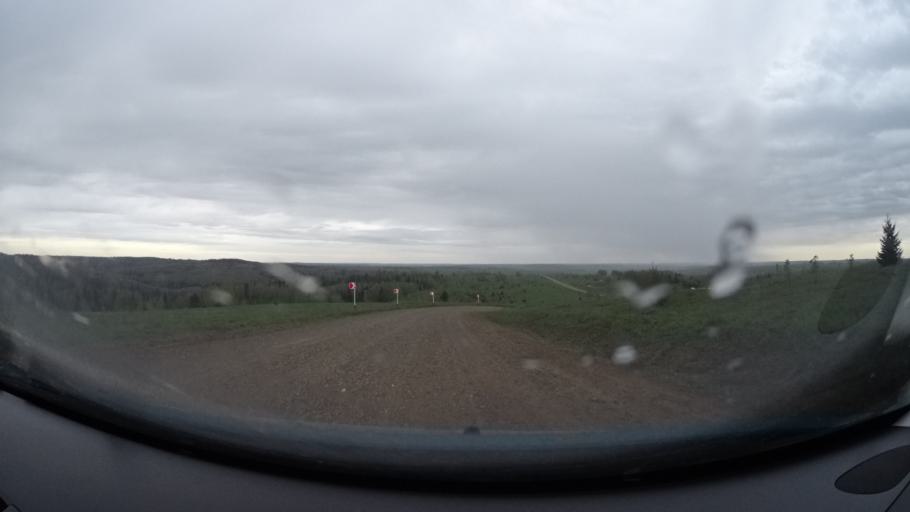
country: RU
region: Perm
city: Kuyeda
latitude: 56.5786
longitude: 55.6842
